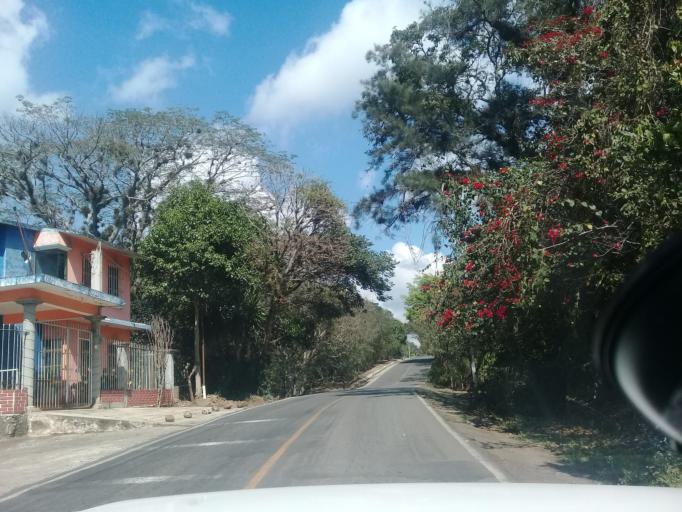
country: MX
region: Veracruz
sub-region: Coatepec
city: Bella Esperanza
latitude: 19.4346
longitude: -96.8681
